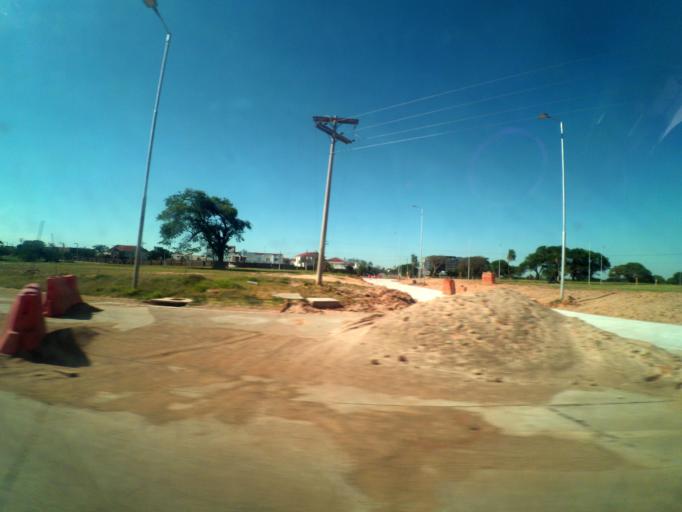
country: BO
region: Santa Cruz
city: Santa Cruz de la Sierra
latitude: -17.7552
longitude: -63.2184
